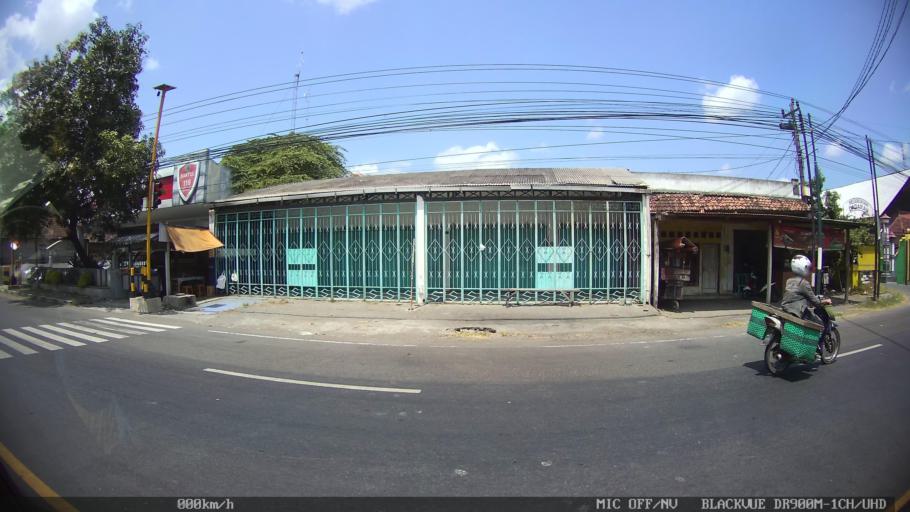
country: ID
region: Daerah Istimewa Yogyakarta
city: Pandak
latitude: -7.9060
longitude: 110.3147
